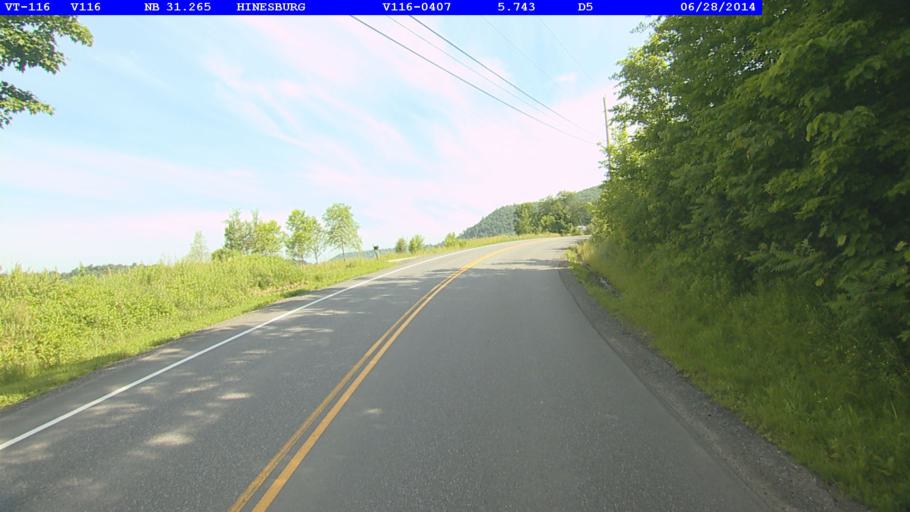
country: US
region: Vermont
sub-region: Chittenden County
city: Hinesburg
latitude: 44.3450
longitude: -73.1187
